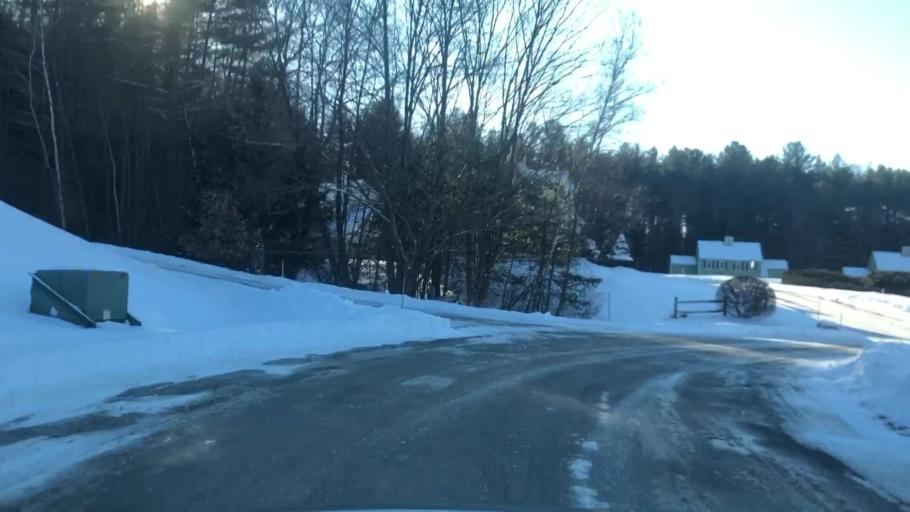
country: US
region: New Hampshire
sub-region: Hillsborough County
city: Milford
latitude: 42.8132
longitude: -71.6892
